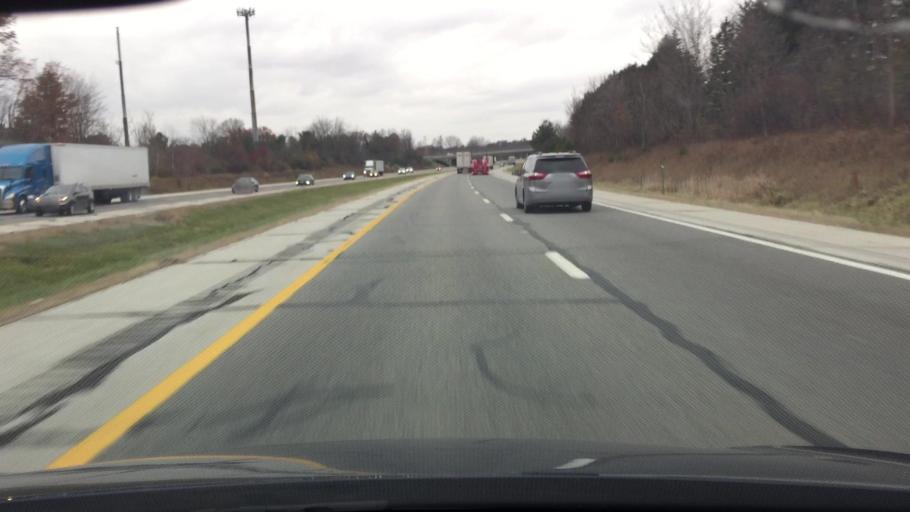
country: US
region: Ohio
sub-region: Mahoning County
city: Canfield
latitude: 41.0394
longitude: -80.7556
